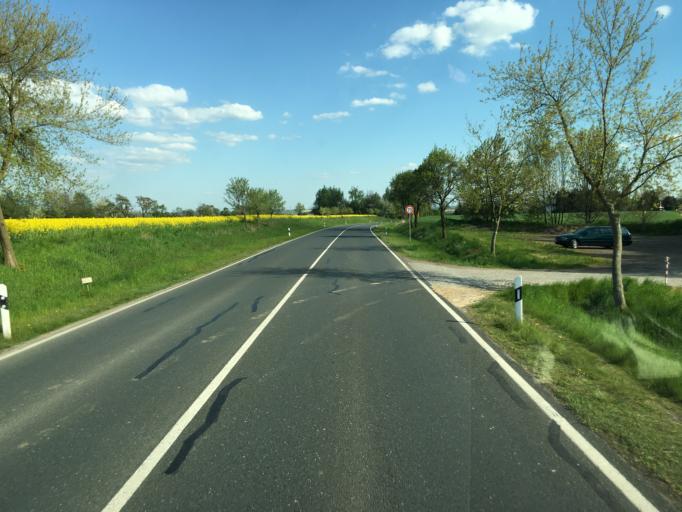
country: DE
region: Saxony
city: Ebersbach
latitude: 51.1054
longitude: 13.0992
